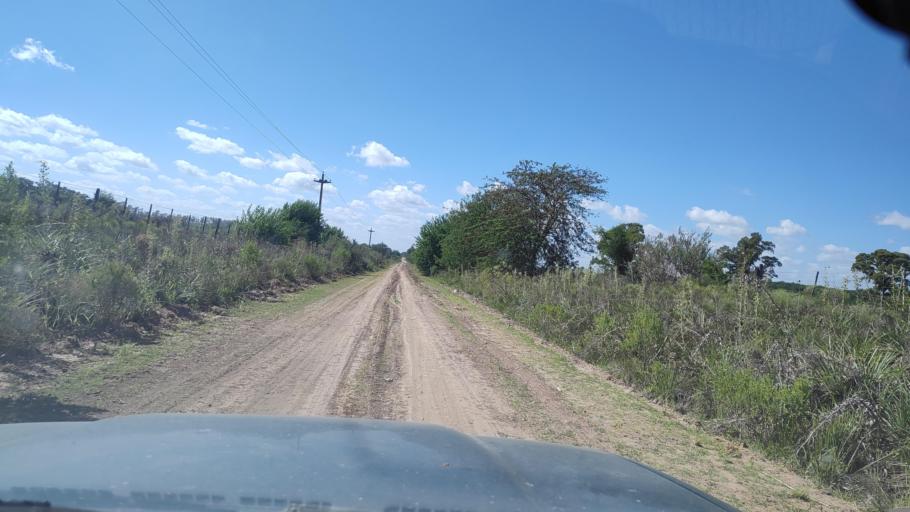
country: AR
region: Buenos Aires
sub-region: Partido de Lujan
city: Lujan
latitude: -34.5178
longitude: -59.1611
